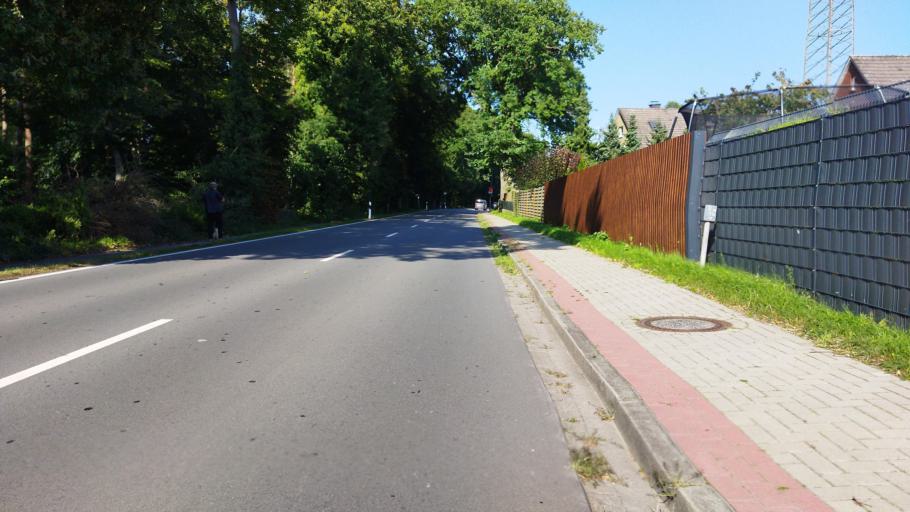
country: DE
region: Lower Saxony
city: Hasbergen
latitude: 52.2620
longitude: 7.9566
